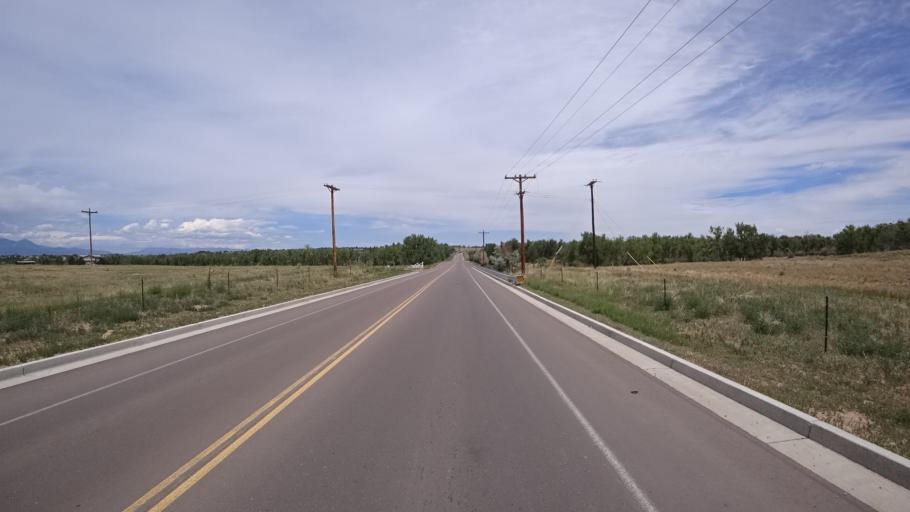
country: US
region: Colorado
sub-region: El Paso County
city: Fountain
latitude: 38.6990
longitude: -104.6737
